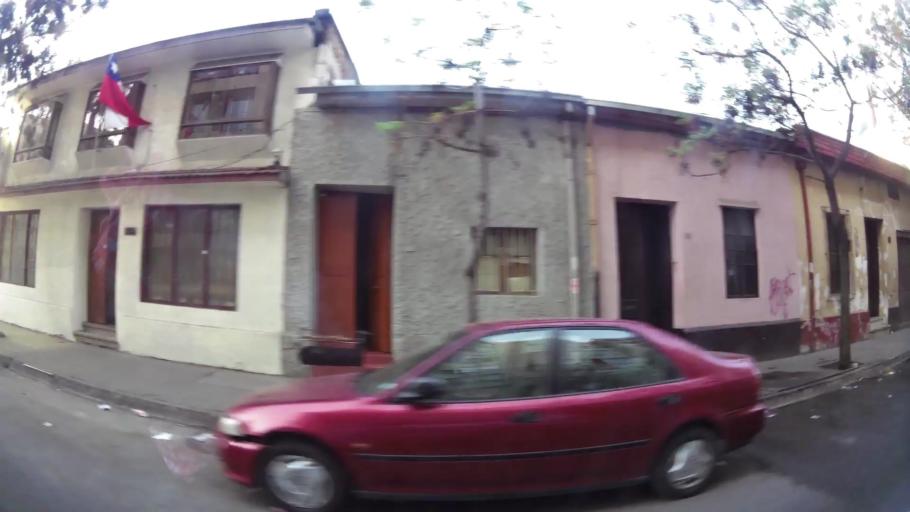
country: CL
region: Santiago Metropolitan
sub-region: Provincia de Santiago
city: Santiago
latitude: -33.4346
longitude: -70.6771
